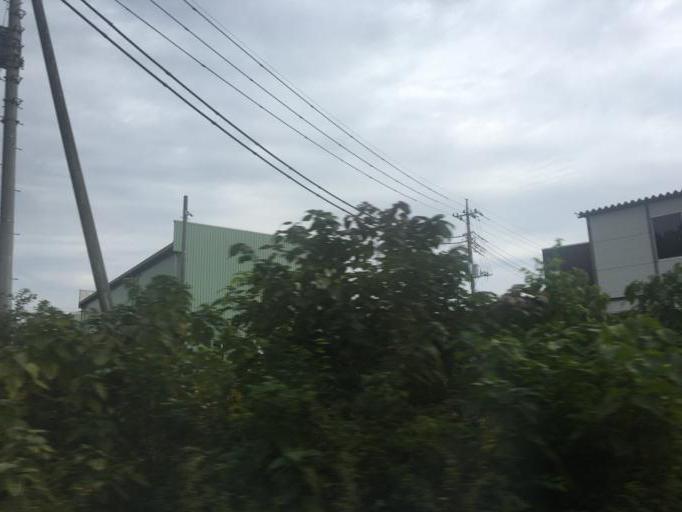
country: JP
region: Tokyo
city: Fussa
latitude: 35.7839
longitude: 139.3421
